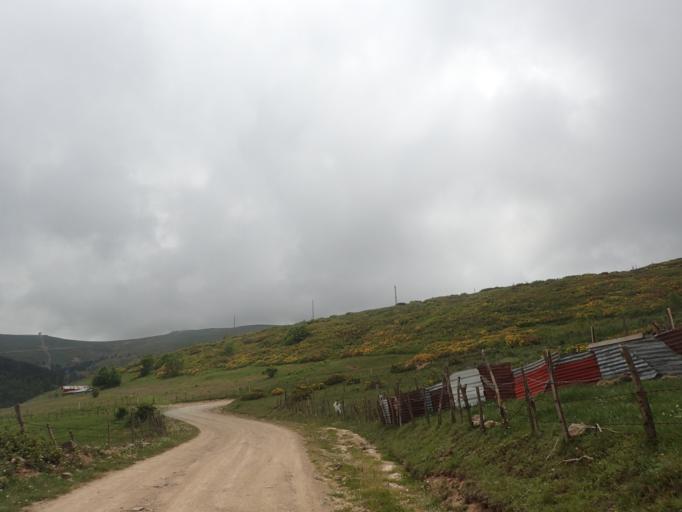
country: TR
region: Ordu
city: Topcam
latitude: 40.6390
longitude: 37.9385
